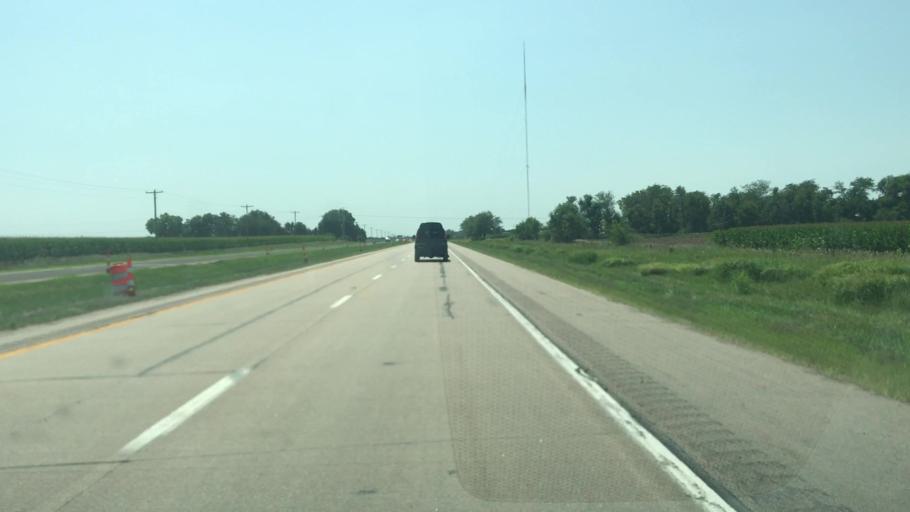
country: US
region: Nebraska
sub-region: Adams County
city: Hastings
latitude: 40.6586
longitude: -98.3824
